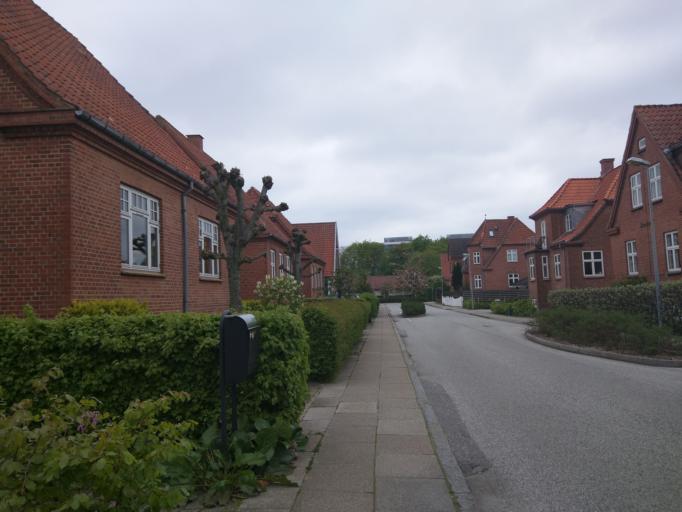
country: DK
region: Central Jutland
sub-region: Viborg Kommune
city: Viborg
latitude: 56.4449
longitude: 9.3988
